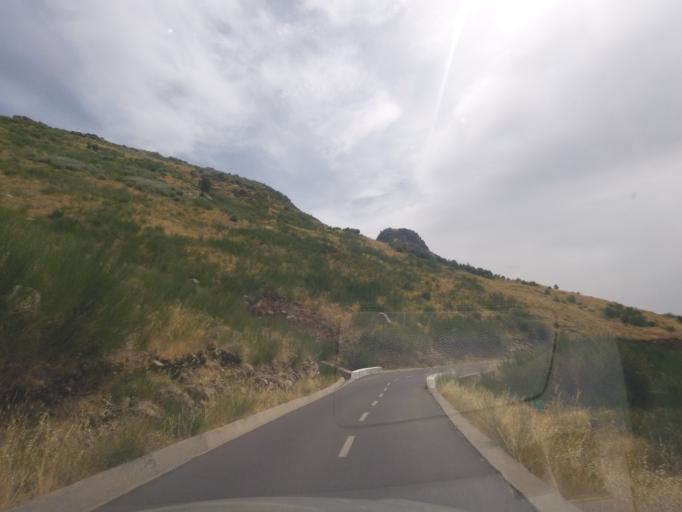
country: PT
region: Madeira
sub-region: Camara de Lobos
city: Curral das Freiras
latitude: 32.7250
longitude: -16.9358
